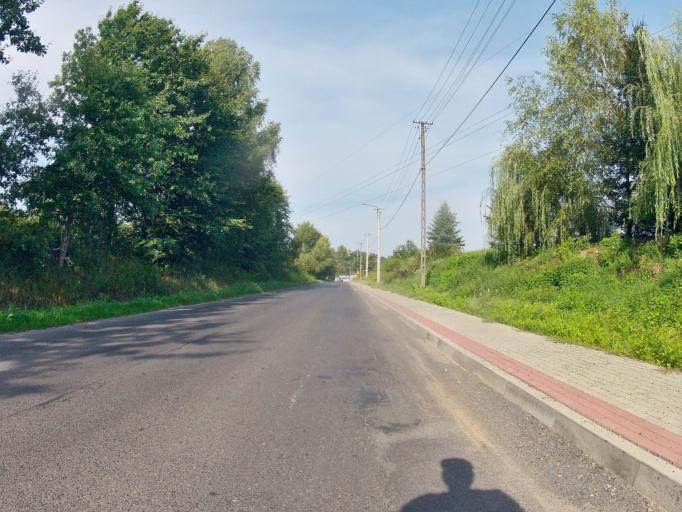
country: PL
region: Subcarpathian Voivodeship
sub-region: Powiat jasielski
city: Trzcinica
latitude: 49.7624
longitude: 21.4295
